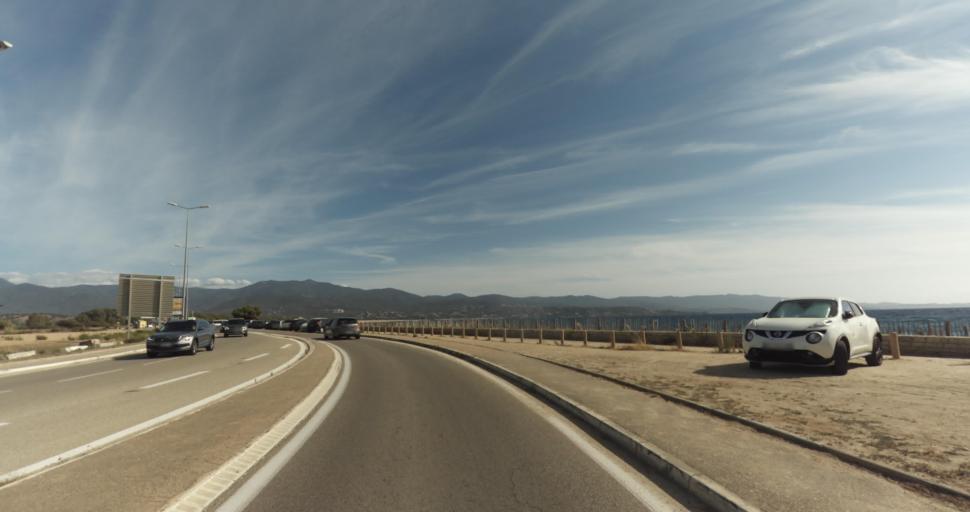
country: FR
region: Corsica
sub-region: Departement de la Corse-du-Sud
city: Ajaccio
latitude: 41.9262
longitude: 8.7787
